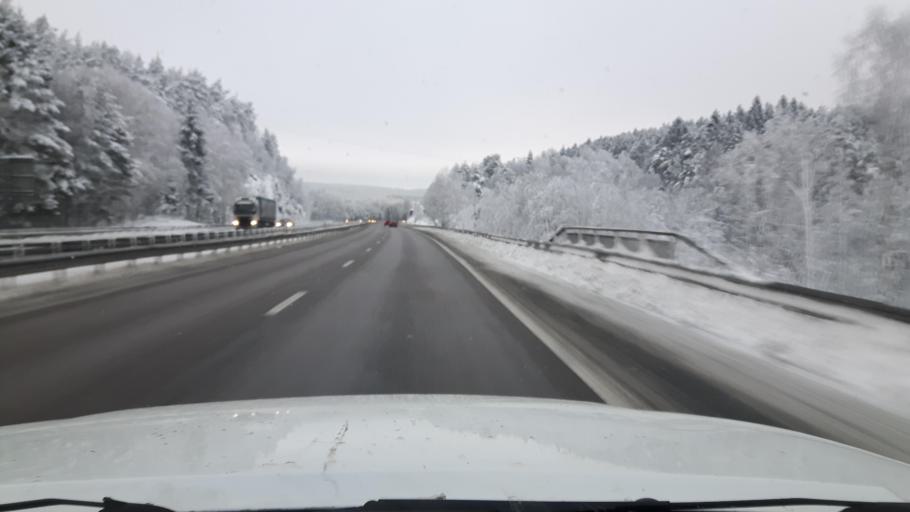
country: SE
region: Halland
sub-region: Kungsbacka Kommun
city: Fjaeras kyrkby
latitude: 57.4007
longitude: 12.1850
